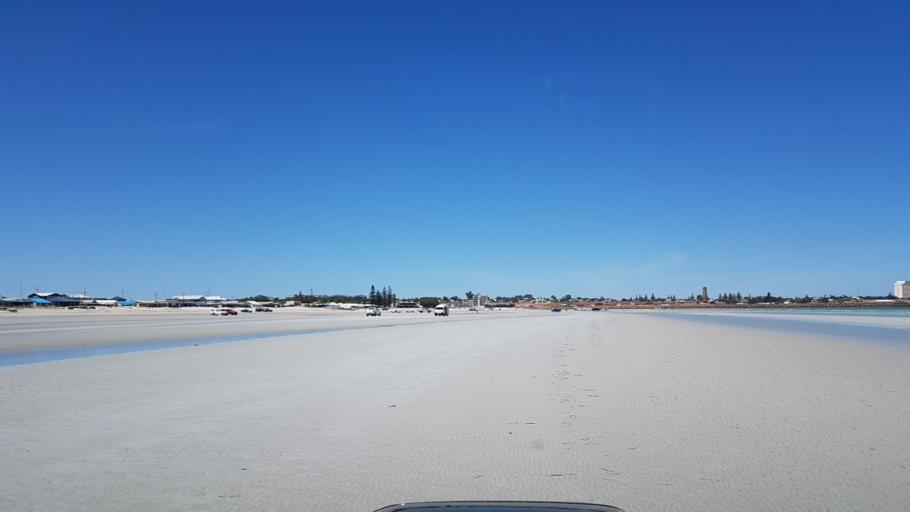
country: AU
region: South Australia
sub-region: Copper Coast
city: Wallaroo
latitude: -33.9134
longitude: 137.6295
